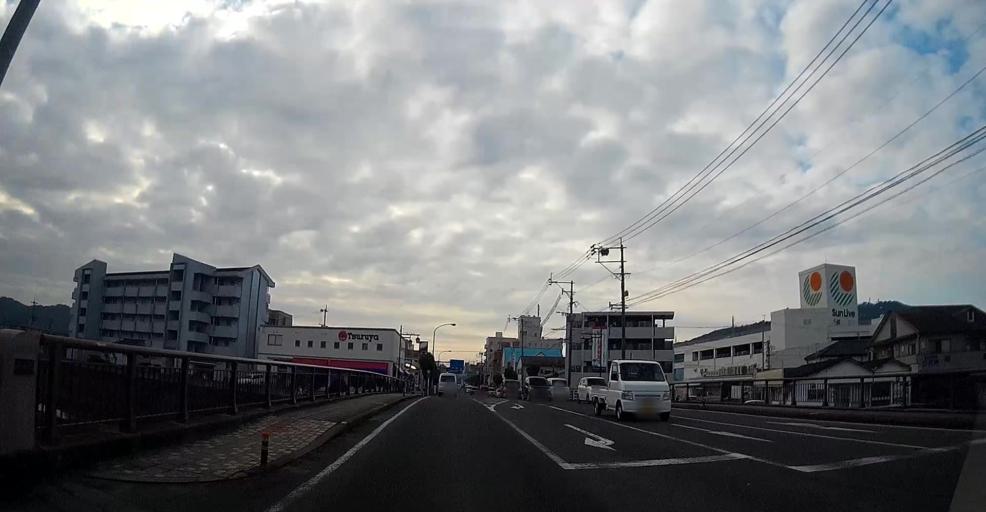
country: JP
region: Kumamoto
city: Hondo
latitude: 32.4570
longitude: 130.1933
